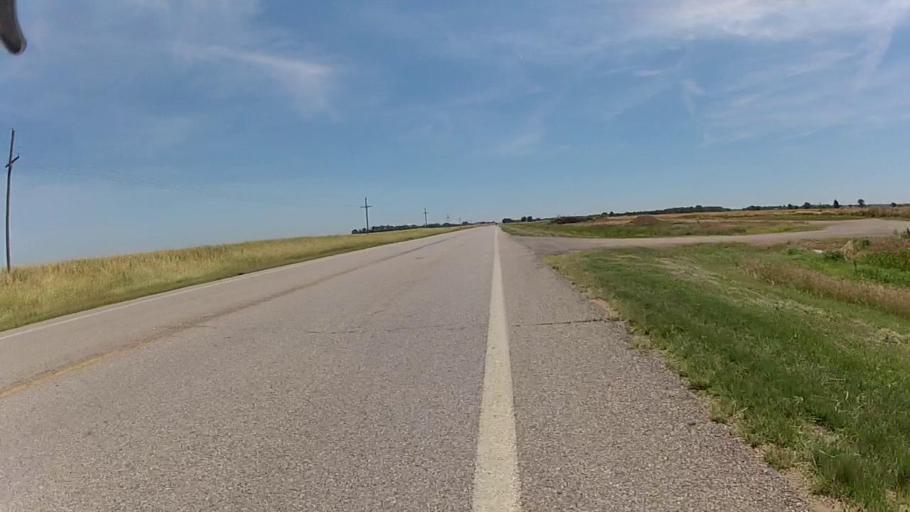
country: US
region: Kansas
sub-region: Barber County
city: Medicine Lodge
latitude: 37.2542
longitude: -98.5054
